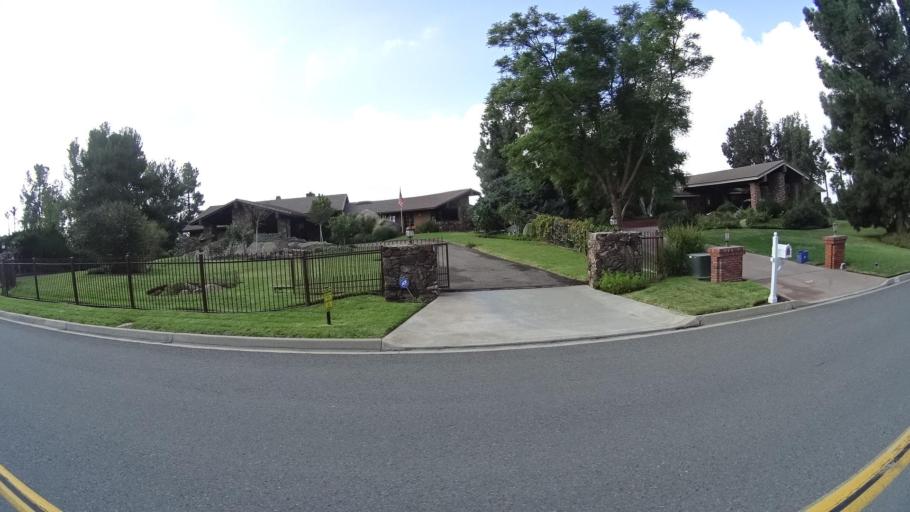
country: US
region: California
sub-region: San Diego County
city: Granite Hills
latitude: 32.7743
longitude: -116.8980
